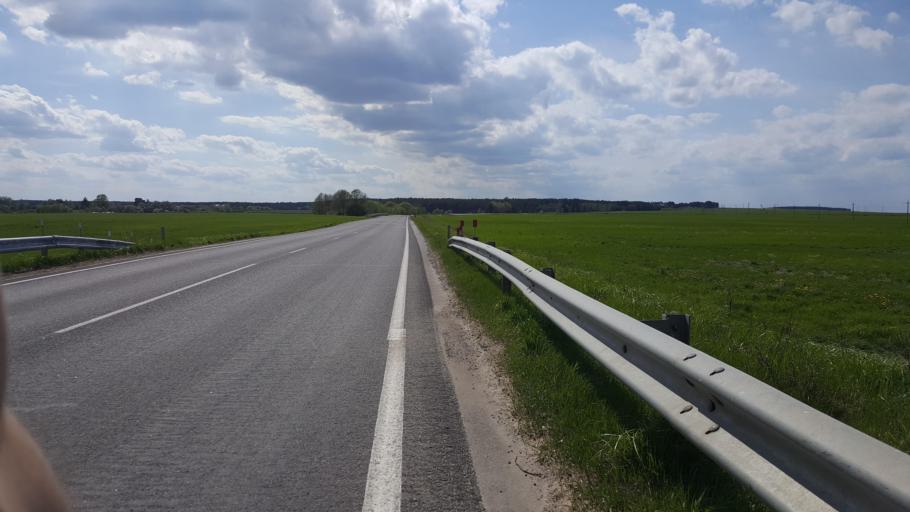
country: BY
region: Brest
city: Kamyanyets
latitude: 52.4007
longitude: 23.8956
